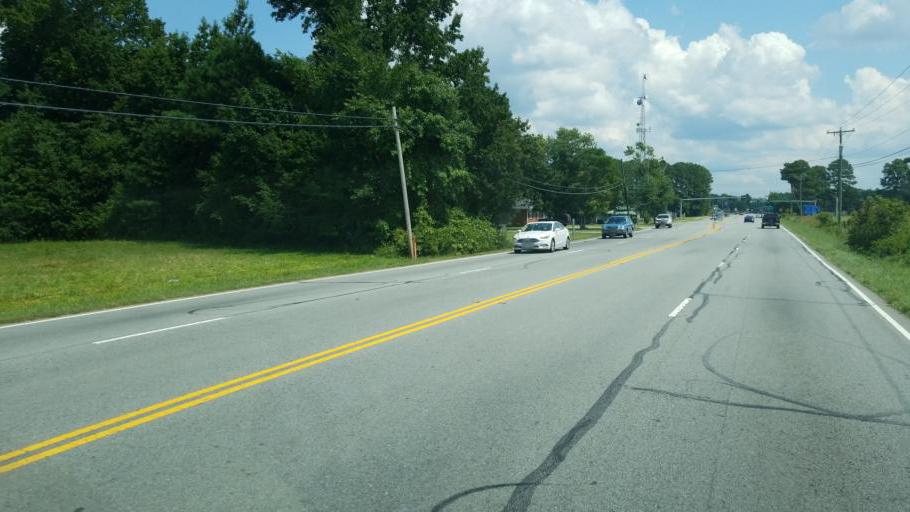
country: US
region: Virginia
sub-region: City of Suffolk
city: Suffolk
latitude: 36.7724
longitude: -76.6123
